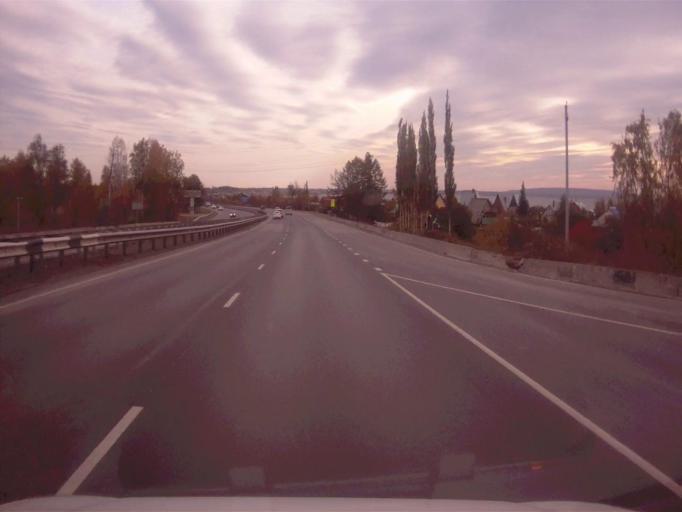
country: RU
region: Chelyabinsk
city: Novosineglazovskiy
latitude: 55.0373
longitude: 61.4415
